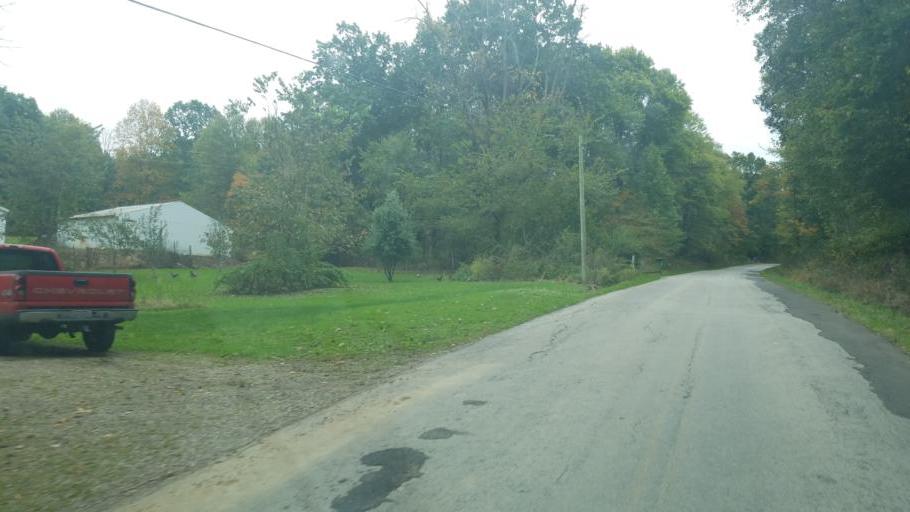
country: US
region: Ohio
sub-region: Wayne County
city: Shreve
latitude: 40.5762
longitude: -82.1090
